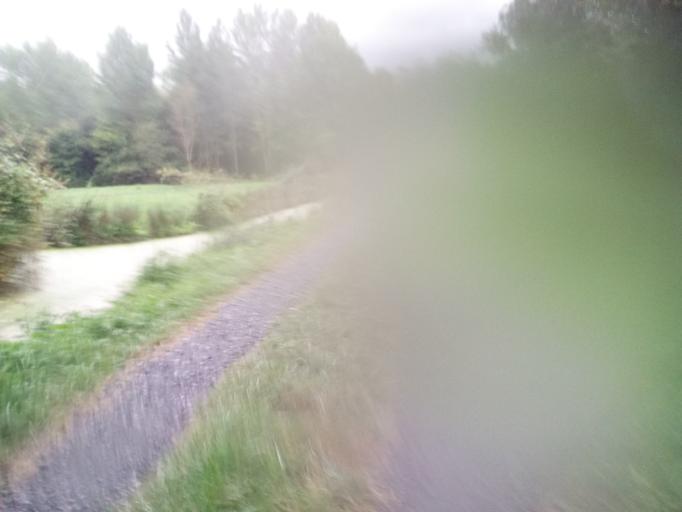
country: FR
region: Lower Normandy
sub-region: Departement du Calvados
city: Bavent
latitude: 49.2341
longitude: -0.1612
